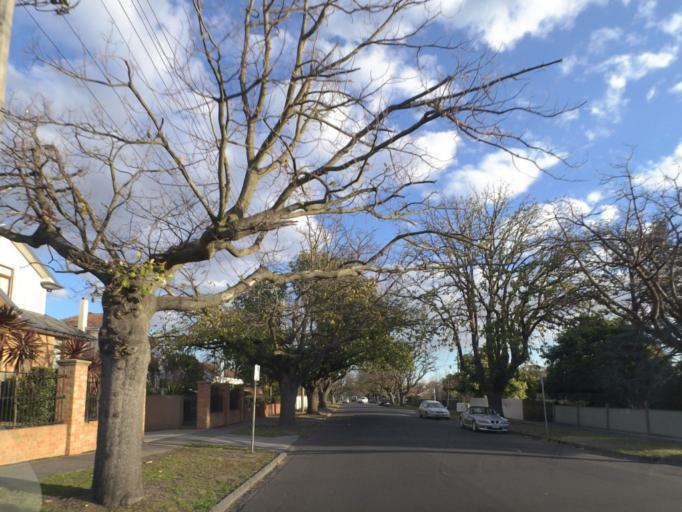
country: AU
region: Victoria
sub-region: Whitehorse
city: Surrey Hills
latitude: -37.8373
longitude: 145.0931
